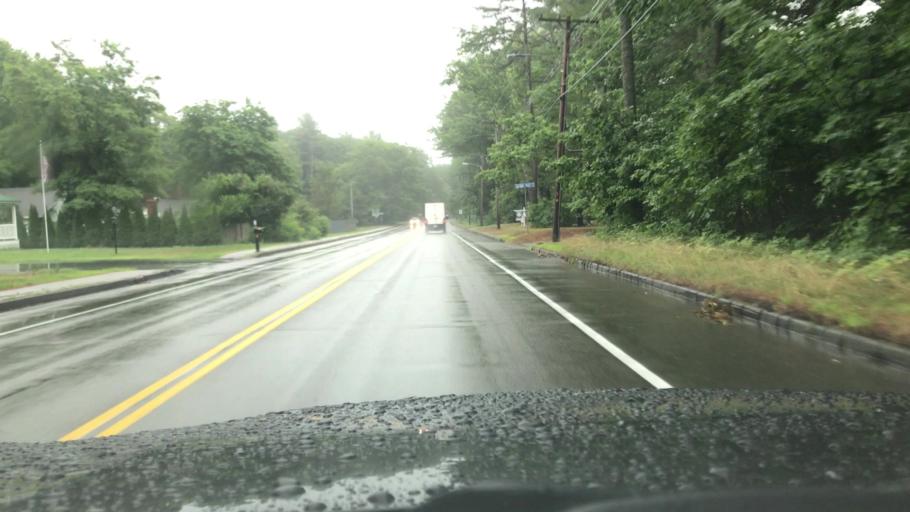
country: US
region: Maine
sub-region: York County
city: Kennebunk
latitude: 43.4021
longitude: -70.5585
